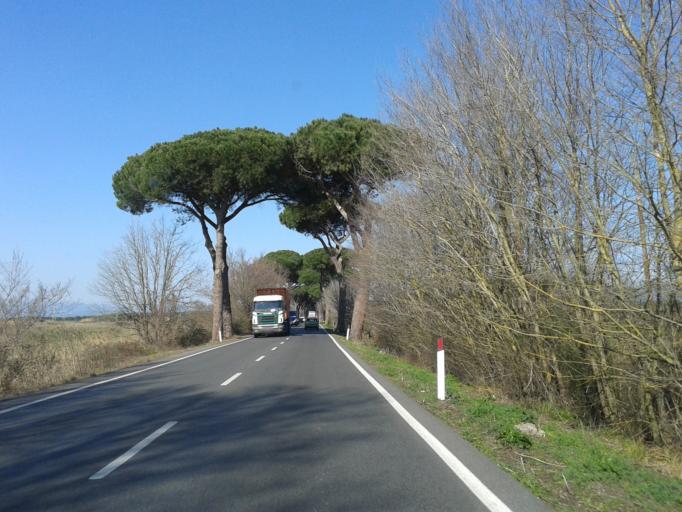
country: IT
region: Tuscany
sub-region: Provincia di Livorno
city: Guasticce
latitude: 43.6466
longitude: 10.3608
